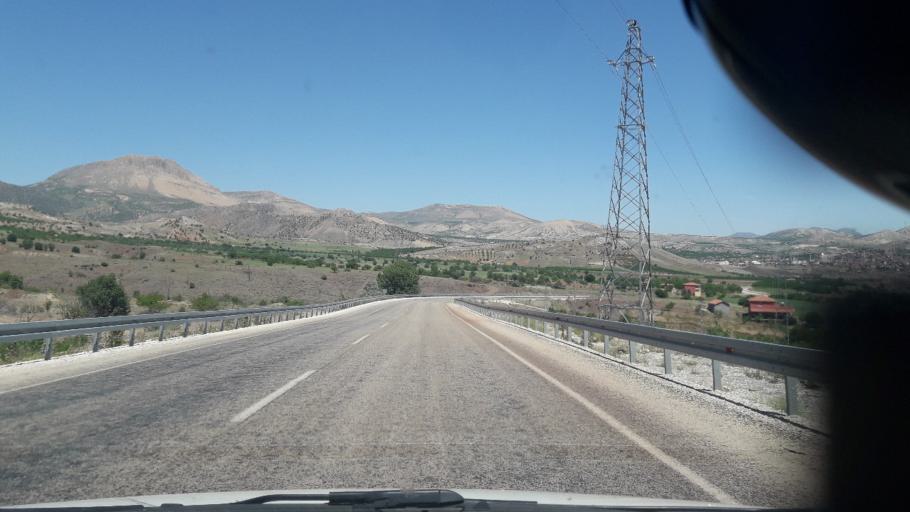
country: TR
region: Malatya
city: Hekimhan
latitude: 38.8217
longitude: 37.8840
